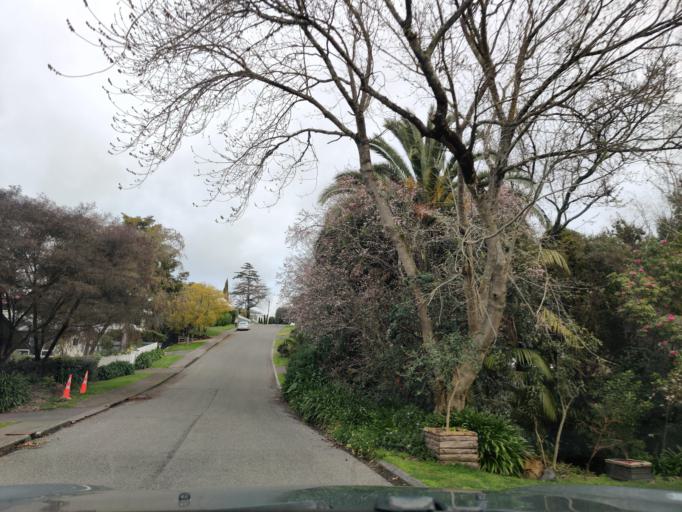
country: NZ
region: Hawke's Bay
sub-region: Hastings District
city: Hastings
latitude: -39.6734
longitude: 176.8857
